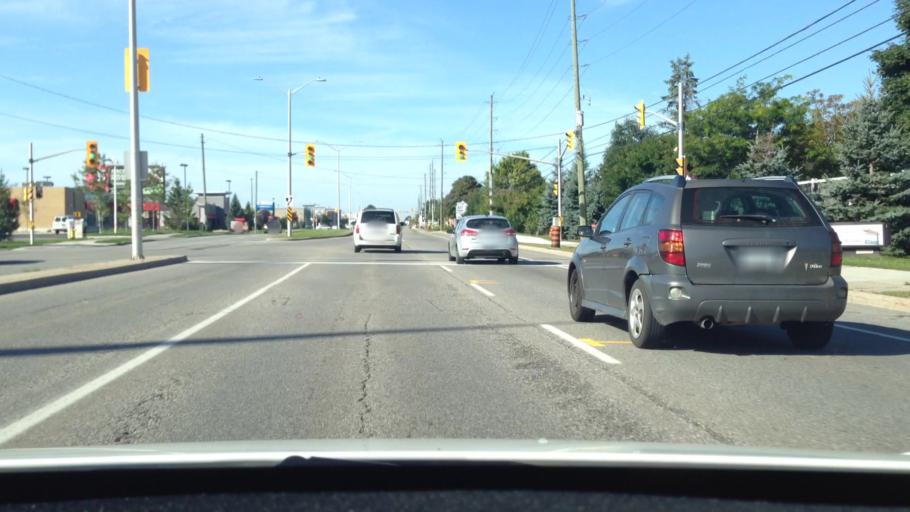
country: CA
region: Ontario
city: Ottawa
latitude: 45.4530
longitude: -75.5069
